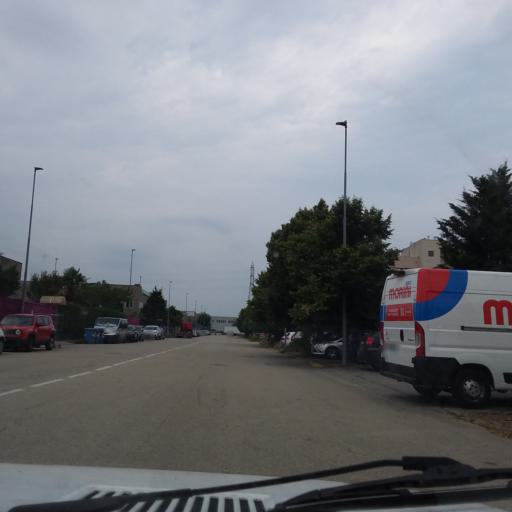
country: IT
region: Piedmont
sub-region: Provincia di Torino
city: Tetti Neirotti
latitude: 45.0615
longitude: 7.5558
